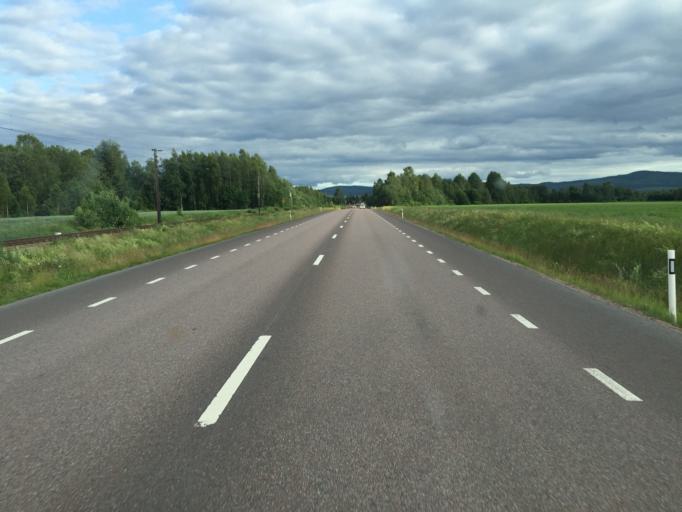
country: SE
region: Dalarna
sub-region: Gagnefs Kommun
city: Djuras
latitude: 60.5722
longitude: 15.1245
